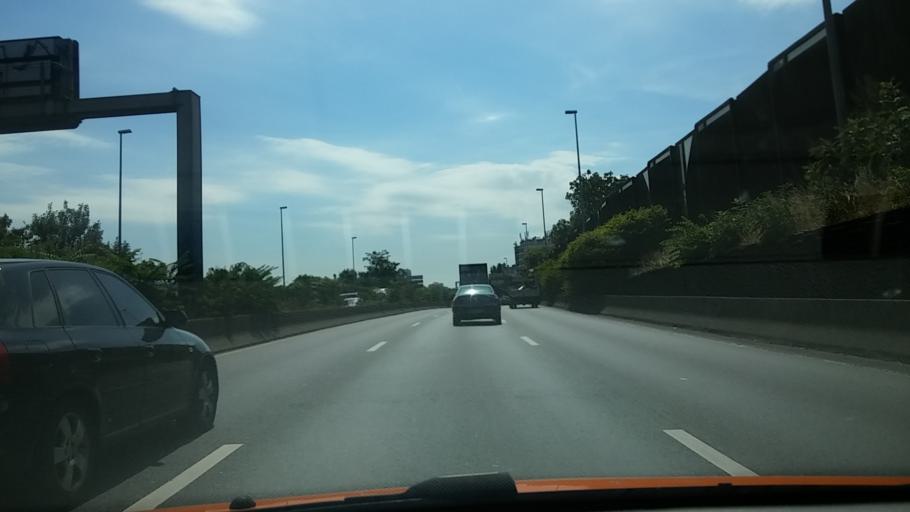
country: FR
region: Ile-de-France
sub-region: Departement du Val-de-Marne
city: Fontenay-sous-Bois
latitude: 48.8696
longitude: 2.4824
